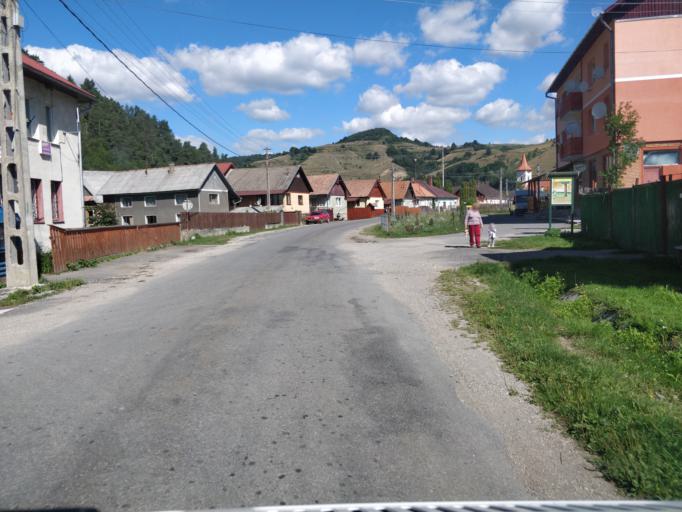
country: RO
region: Cluj
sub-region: Comuna Sacueu
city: Sacuieu
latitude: 46.8208
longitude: 22.8874
